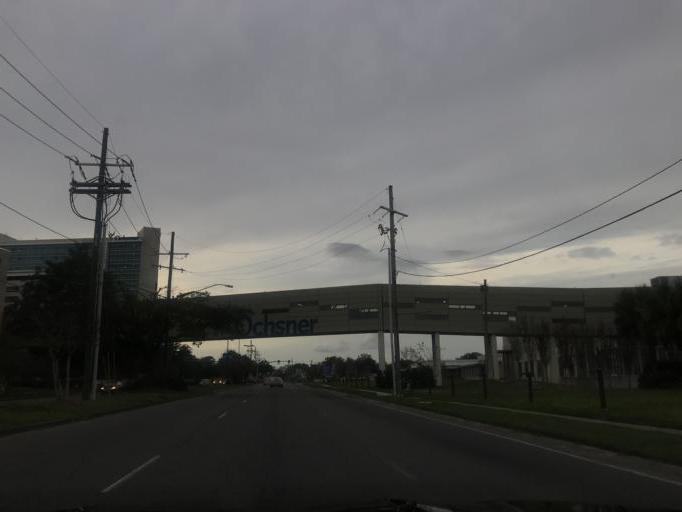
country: US
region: Louisiana
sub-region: Jefferson Parish
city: Jefferson
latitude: 29.9627
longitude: -90.1438
